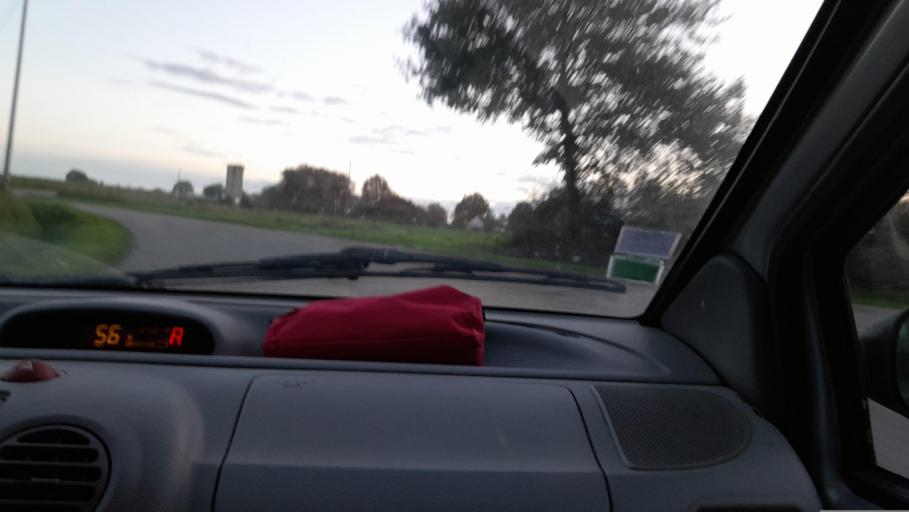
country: FR
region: Brittany
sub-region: Departement d'Ille-et-Vilaine
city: Rannee
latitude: 47.8775
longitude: -1.1835
